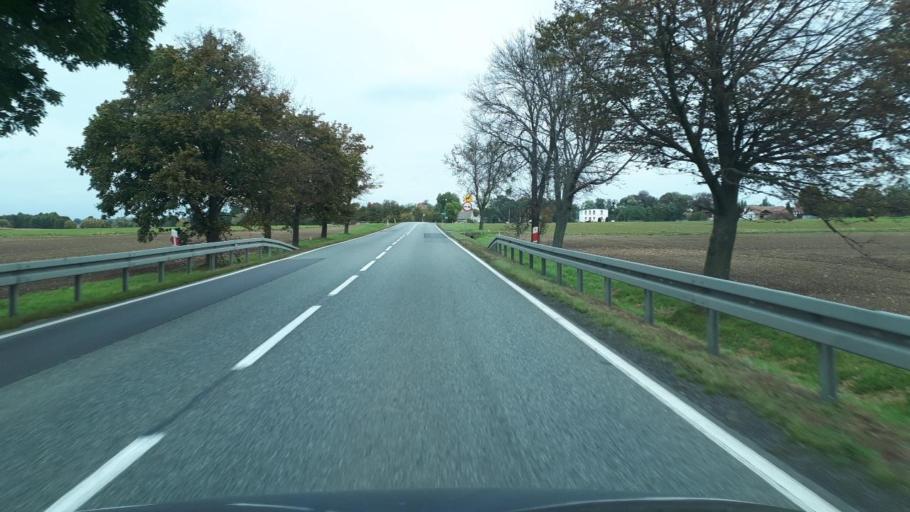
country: PL
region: Opole Voivodeship
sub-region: Powiat kluczborski
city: Byczyna
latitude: 51.0577
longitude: 18.1986
